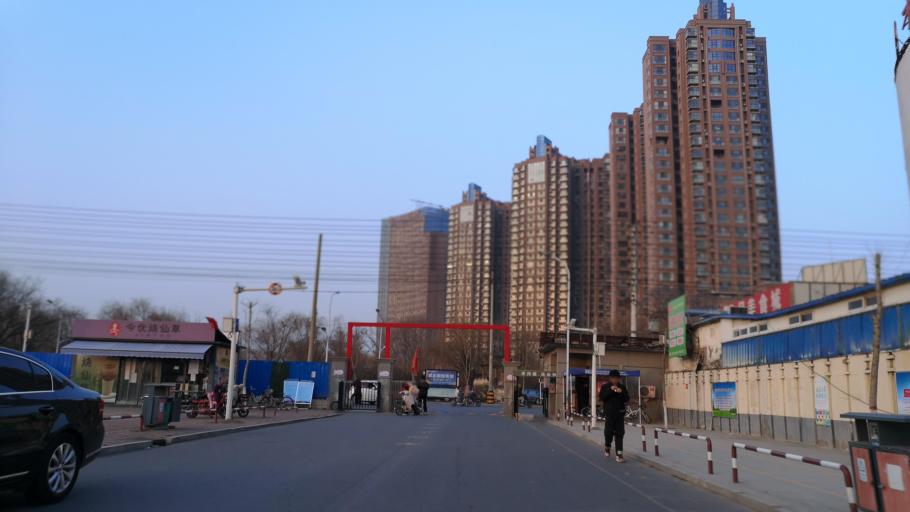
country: CN
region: Henan Sheng
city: Zhongyuanlu
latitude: 35.7711
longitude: 115.0791
